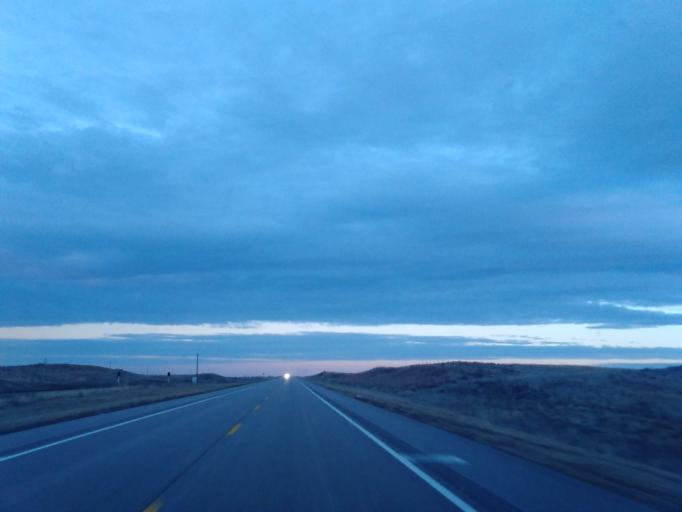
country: US
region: Nebraska
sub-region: Garden County
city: Oshkosh
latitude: 41.3758
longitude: -102.2577
